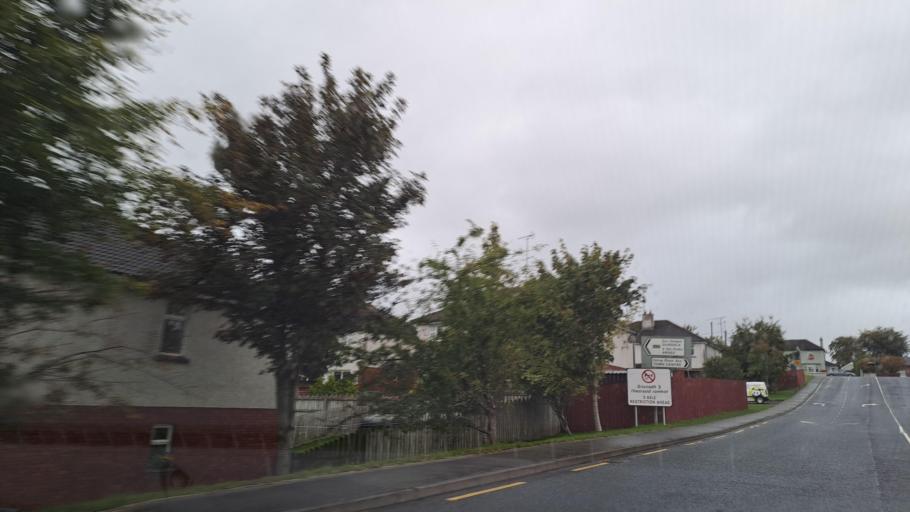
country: IE
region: Ulster
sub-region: County Monaghan
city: Carrickmacross
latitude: 53.9823
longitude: -6.7194
